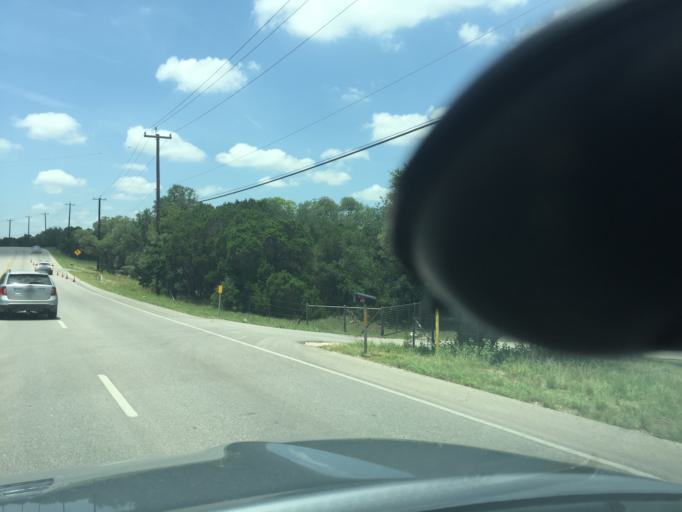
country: US
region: Texas
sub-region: Bexar County
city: Timberwood Park
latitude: 29.7139
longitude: -98.4611
